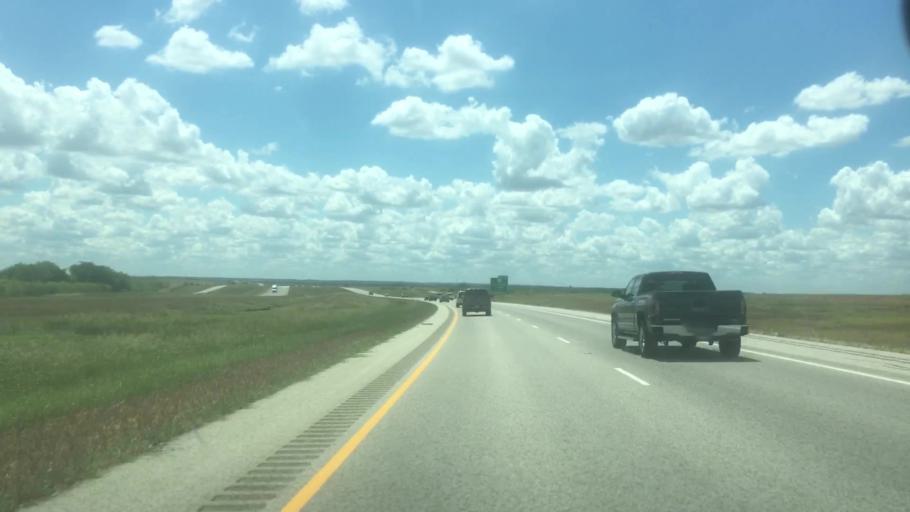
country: US
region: Texas
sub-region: Caldwell County
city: Martindale
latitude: 29.8040
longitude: -97.7760
